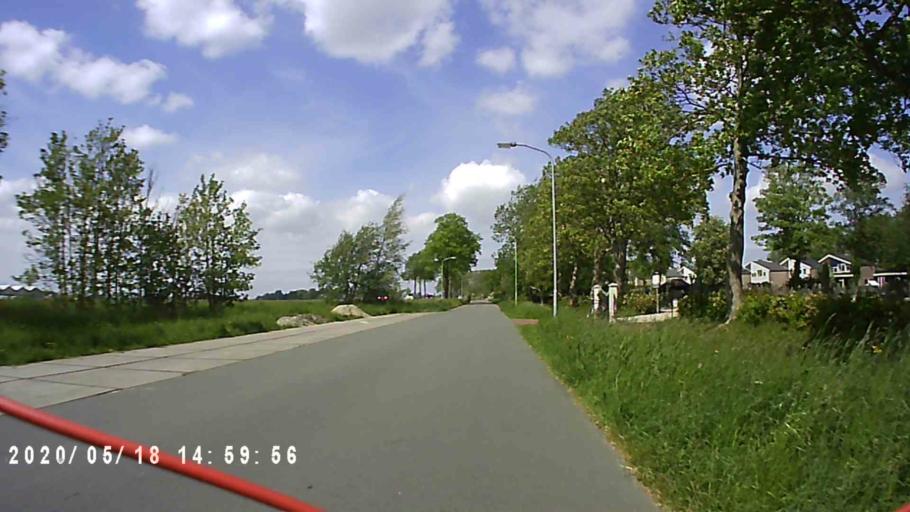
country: NL
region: Groningen
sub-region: Gemeente Winsum
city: Winsum
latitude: 53.3352
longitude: 6.5124
